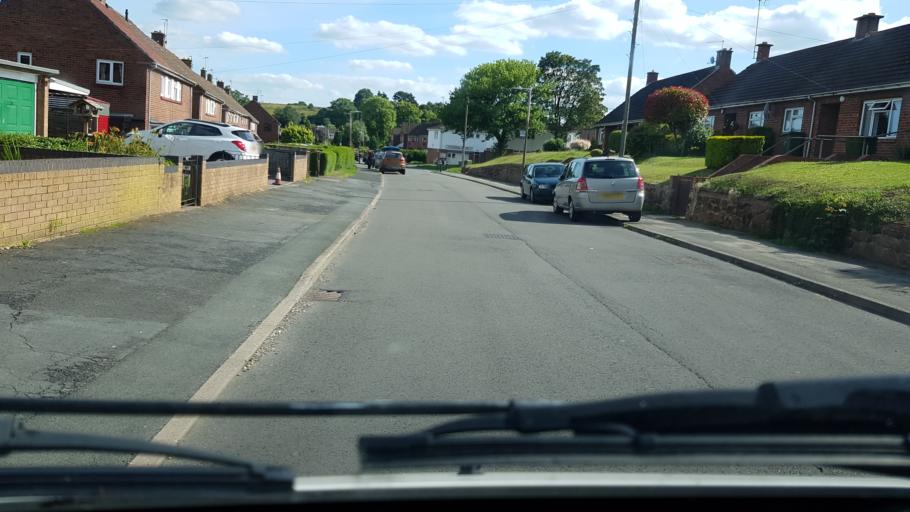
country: GB
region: England
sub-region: Worcestershire
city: Bewdley
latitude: 52.3813
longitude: -2.3049
